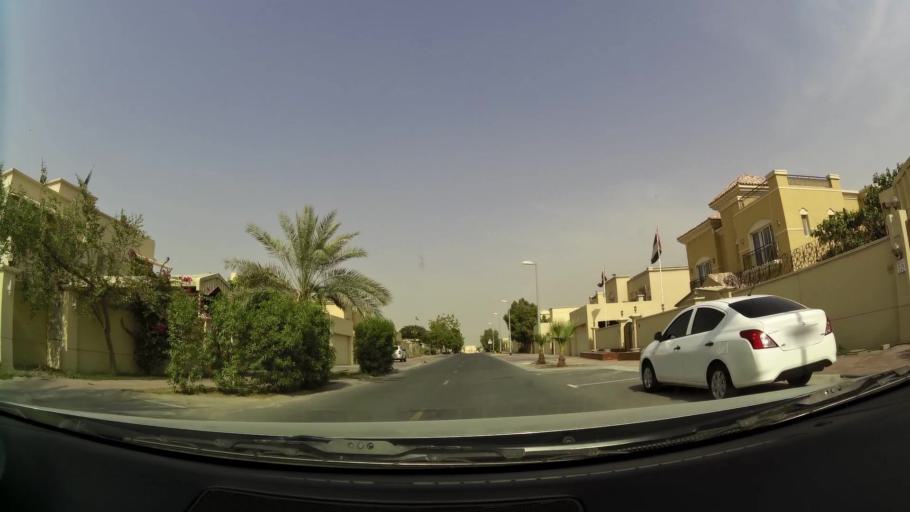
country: AE
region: Ash Shariqah
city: Sharjah
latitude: 25.2622
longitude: 55.4513
